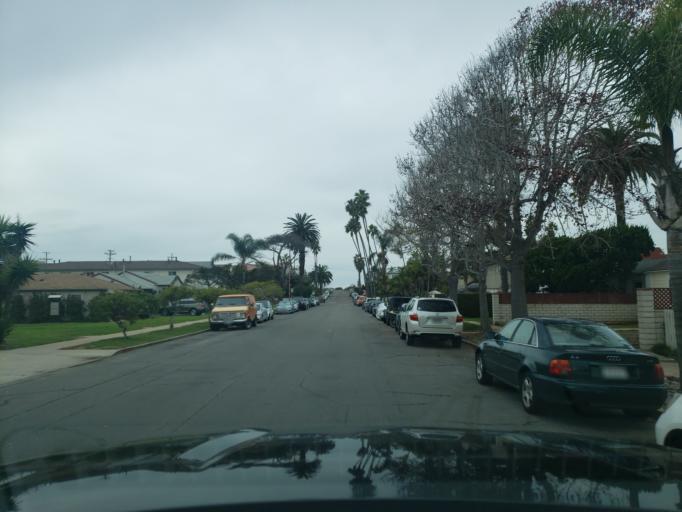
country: US
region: California
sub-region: San Diego County
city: Coronado
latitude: 32.7400
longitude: -117.2525
